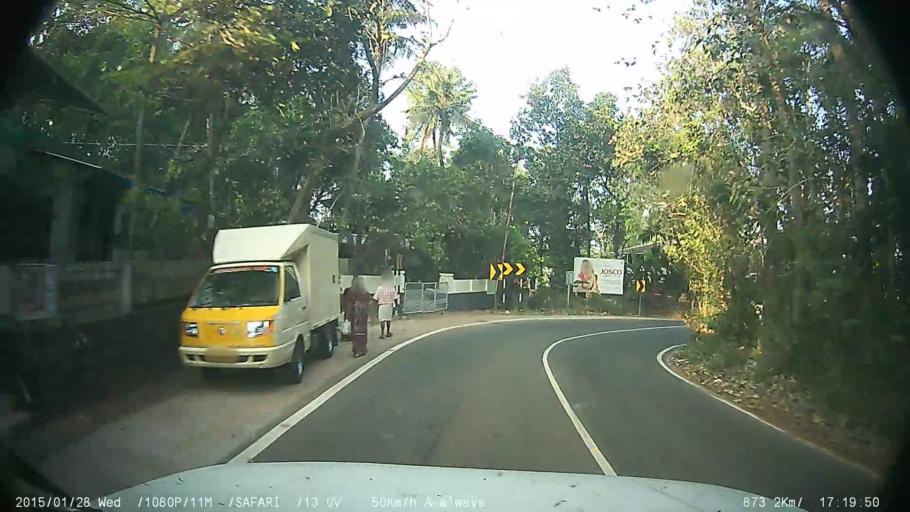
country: IN
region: Kerala
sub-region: Kottayam
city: Kottayam
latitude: 9.5502
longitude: 76.5611
